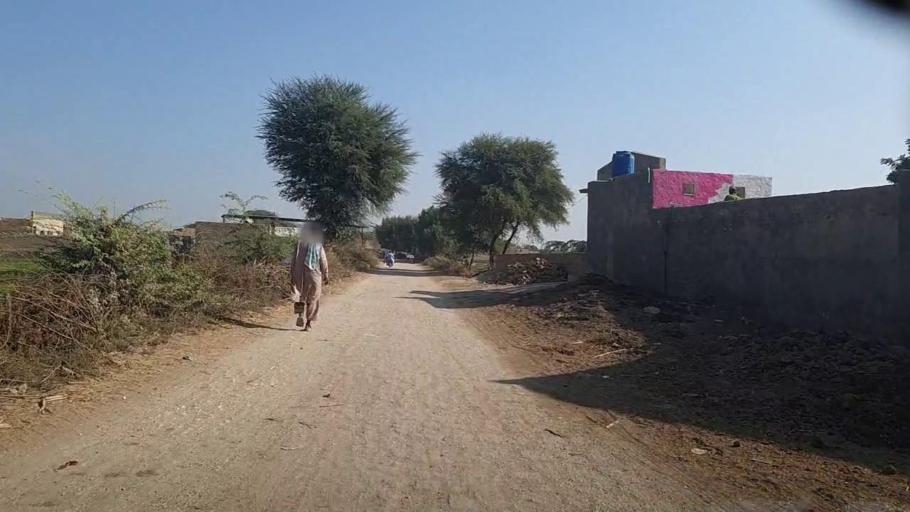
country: PK
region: Sindh
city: Darya Khan Marri
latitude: 26.6727
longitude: 68.3191
